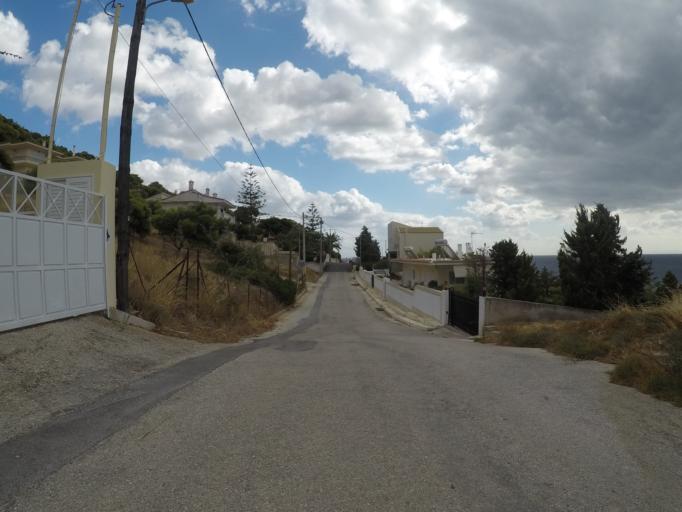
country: GR
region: Attica
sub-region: Nomarchia Anatolikis Attikis
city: Agia Marina
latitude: 37.8109
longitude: 23.8475
